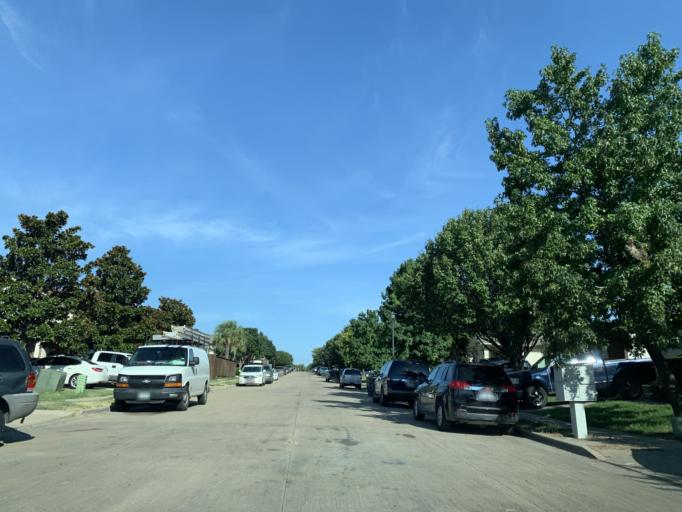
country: US
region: Texas
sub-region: Dallas County
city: Cockrell Hill
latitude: 32.7075
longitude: -96.8995
